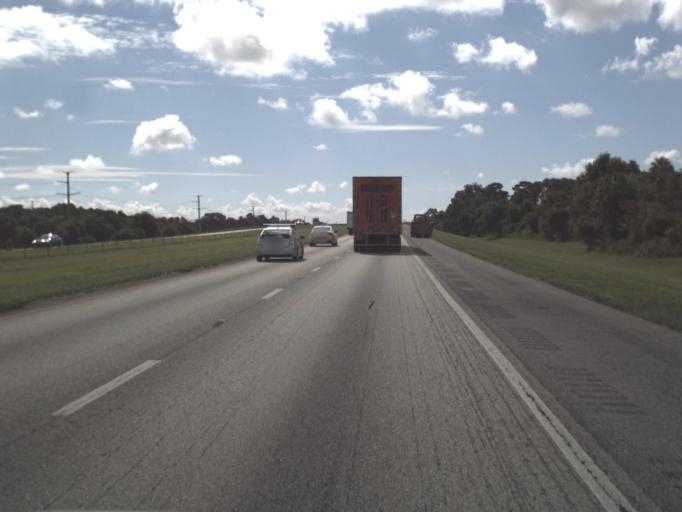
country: US
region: Florida
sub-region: Charlotte County
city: Port Charlotte
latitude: 27.0629
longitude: -82.0886
